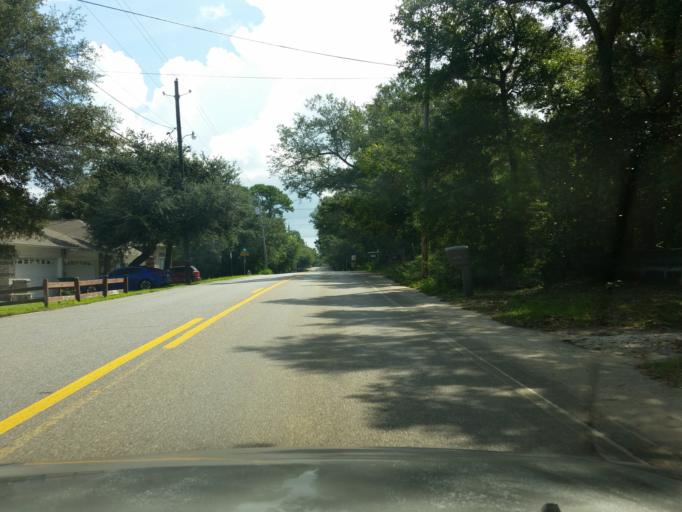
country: US
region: Alabama
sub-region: Baldwin County
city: Orange Beach
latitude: 30.3144
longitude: -87.4495
